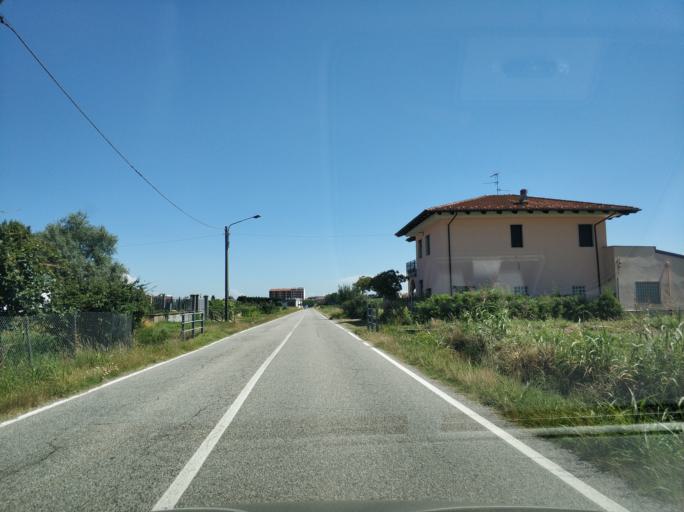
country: IT
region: Piedmont
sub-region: Provincia di Vercelli
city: Cigliano
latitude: 45.3173
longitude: 8.0190
